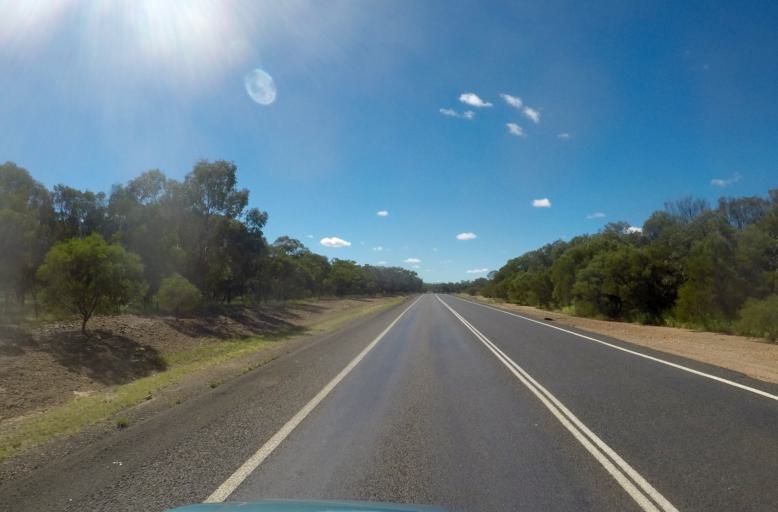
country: AU
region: Queensland
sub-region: Maranoa
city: Roma
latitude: -26.5958
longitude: 149.2835
